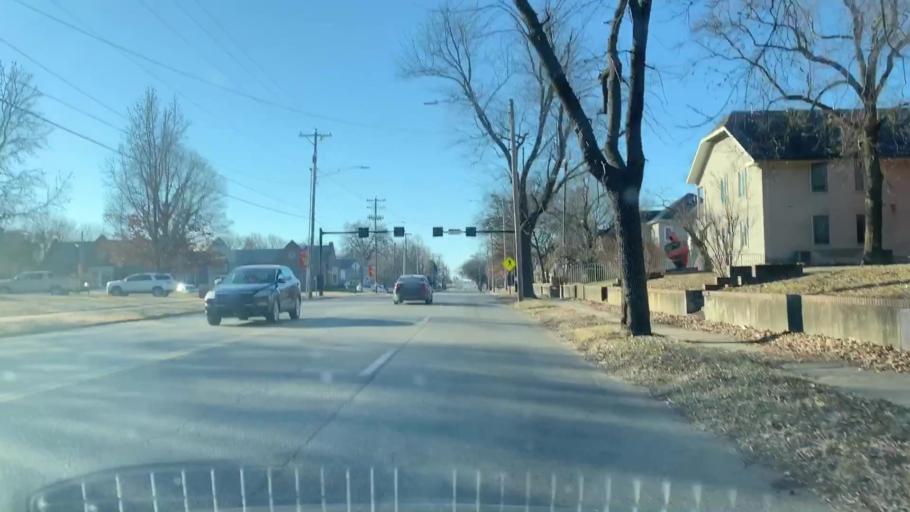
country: US
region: Kansas
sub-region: Crawford County
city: Pittsburg
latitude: 37.3911
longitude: -94.7051
